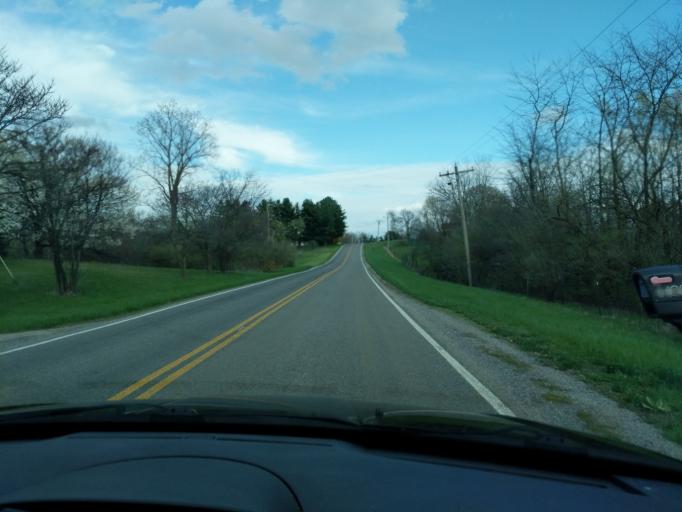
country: US
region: Ohio
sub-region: Champaign County
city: Urbana
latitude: 40.1558
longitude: -83.6598
